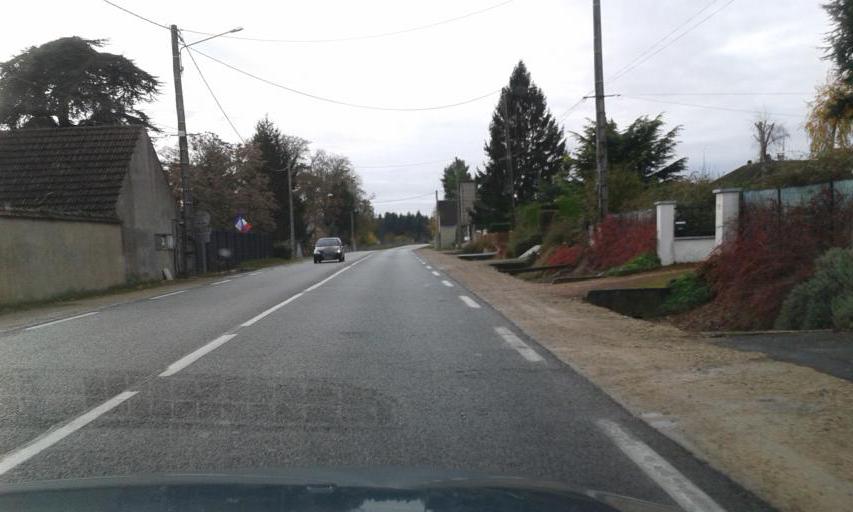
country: FR
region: Centre
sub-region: Departement du Loiret
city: Saint-Ay
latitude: 47.8503
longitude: 1.7350
